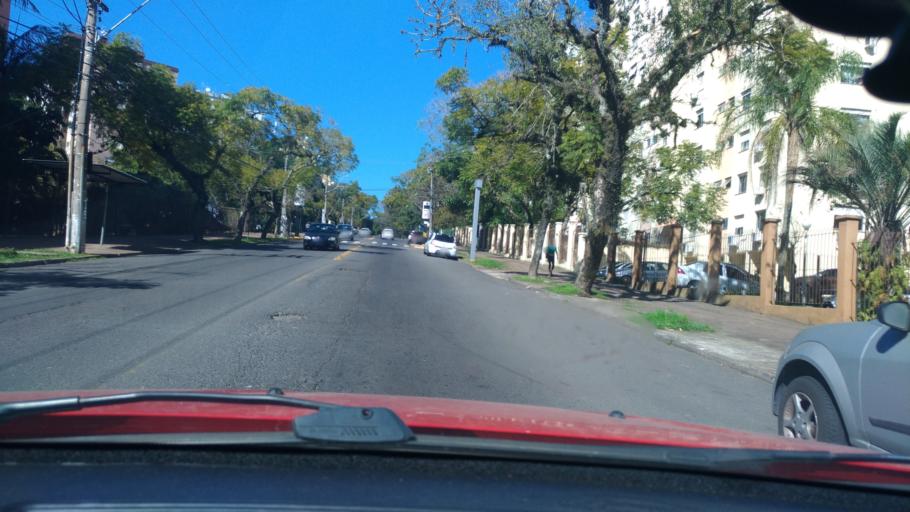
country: BR
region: Rio Grande do Sul
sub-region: Porto Alegre
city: Porto Alegre
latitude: -30.0391
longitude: -51.1451
